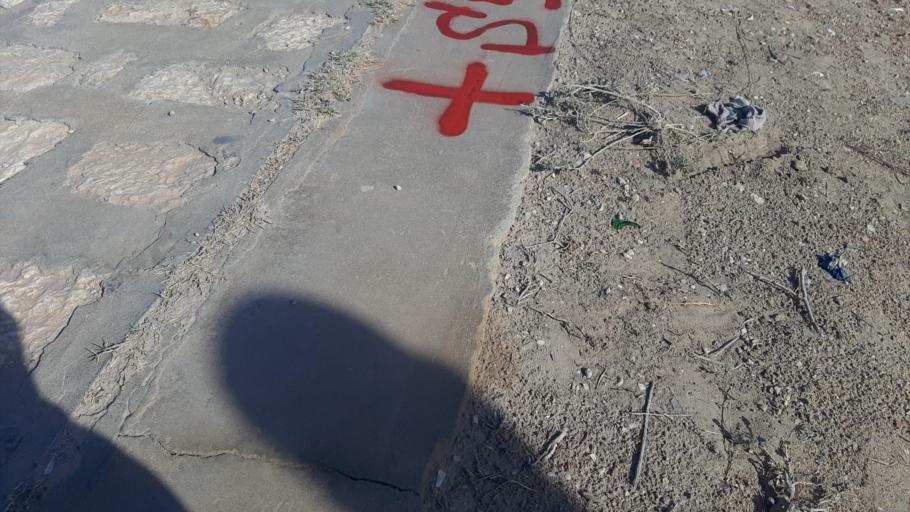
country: TN
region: Qabis
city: Gabes
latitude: 33.8732
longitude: 10.0991
